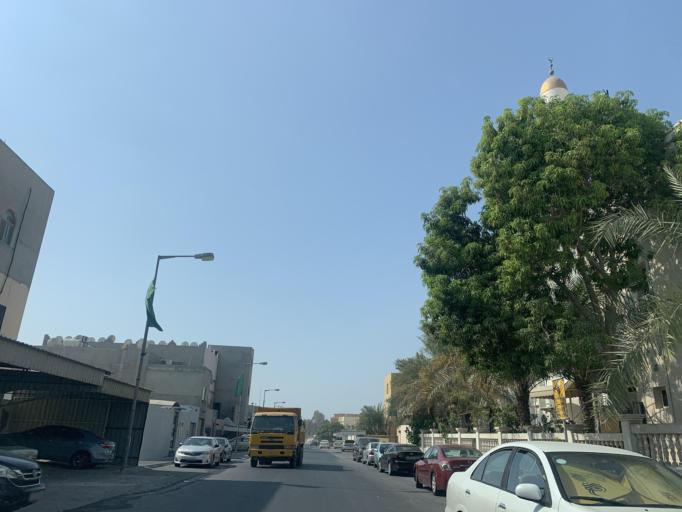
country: BH
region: Central Governorate
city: Madinat Hamad
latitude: 26.1297
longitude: 50.4948
